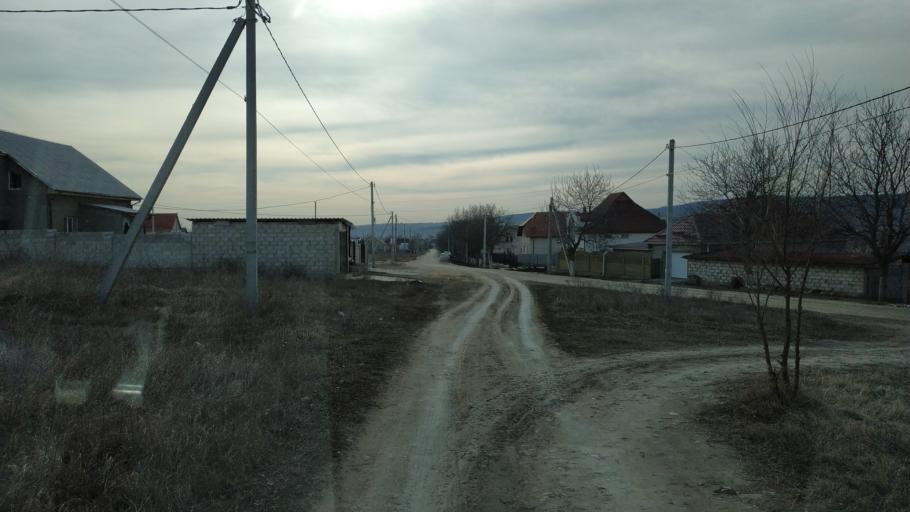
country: MD
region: Chisinau
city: Vatra
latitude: 46.9914
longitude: 28.6665
